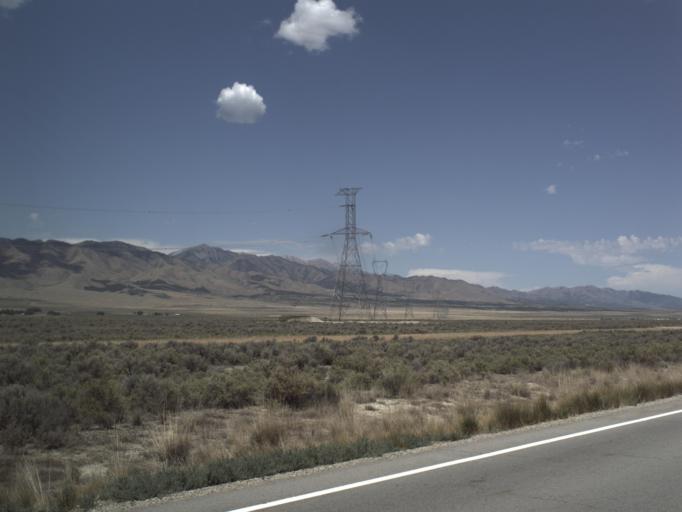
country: US
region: Utah
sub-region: Tooele County
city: Tooele
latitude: 40.3425
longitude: -112.4106
